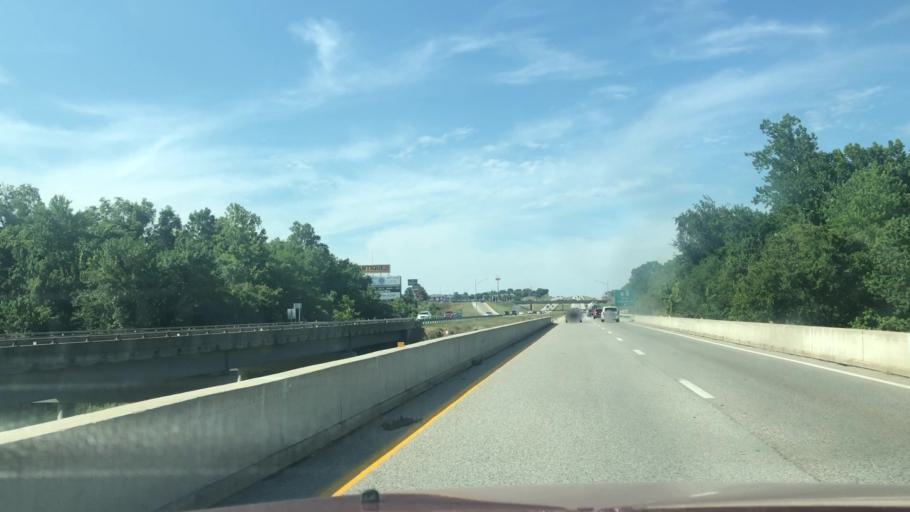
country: US
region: Missouri
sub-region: Christian County
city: Ozark
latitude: 37.0170
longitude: -93.2290
